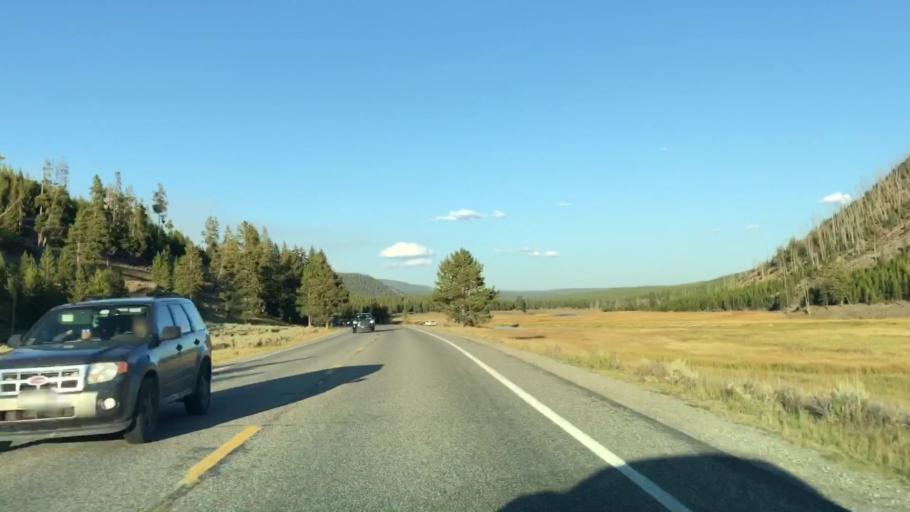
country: US
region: Montana
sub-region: Gallatin County
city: West Yellowstone
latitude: 44.6409
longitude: -110.8799
